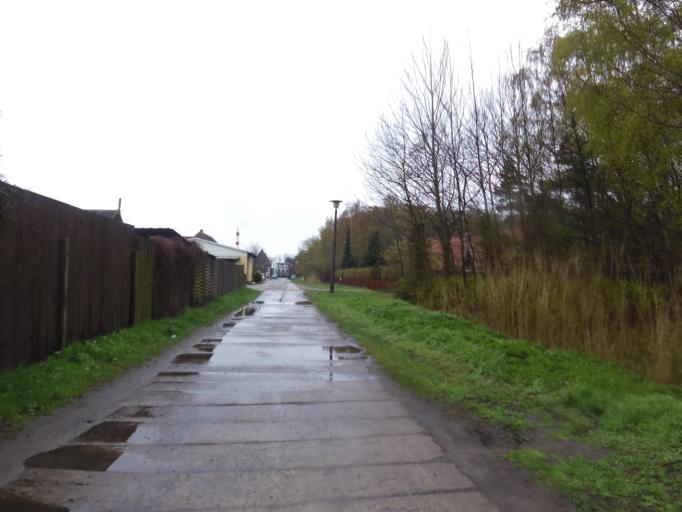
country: DE
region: Mecklenburg-Vorpommern
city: Zingst
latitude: 54.4339
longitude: 12.7078
